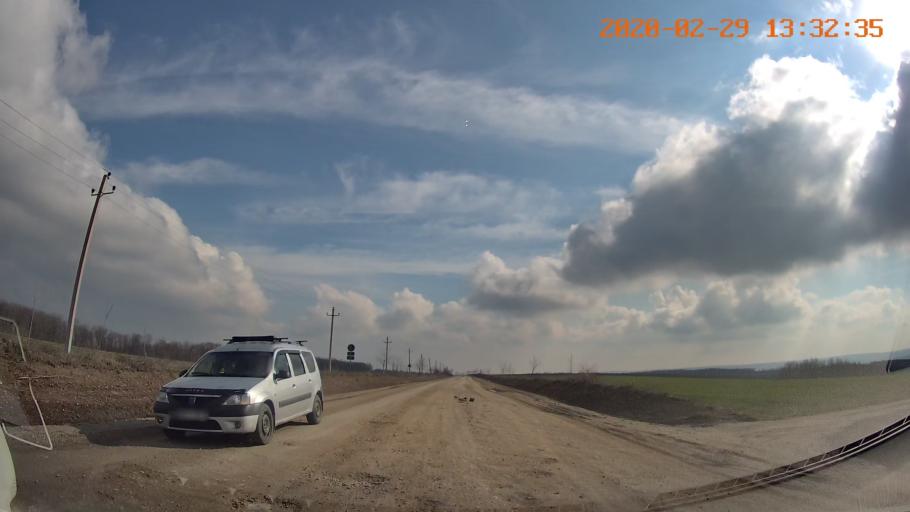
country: MD
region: Telenesti
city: Camenca
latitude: 47.8782
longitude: 28.6109
